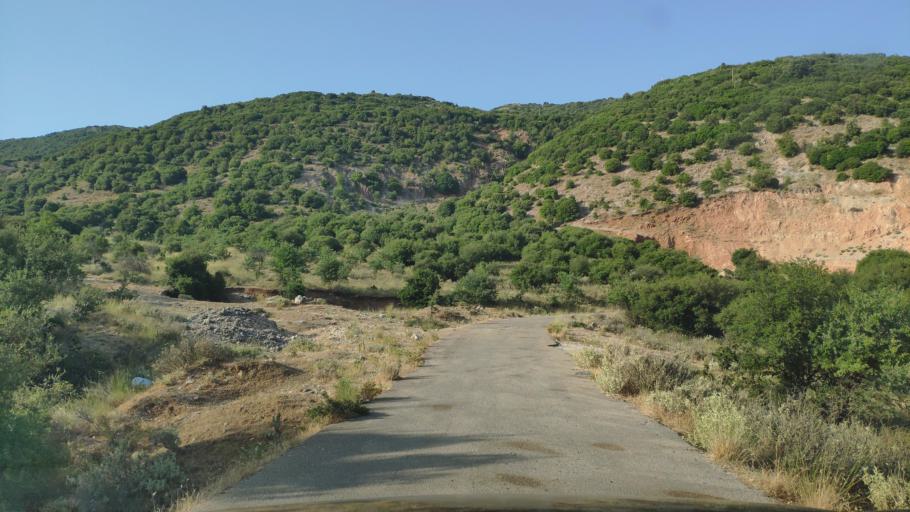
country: GR
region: West Greece
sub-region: Nomos Aitolias kai Akarnanias
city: Monastirakion
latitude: 38.8456
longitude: 20.9816
